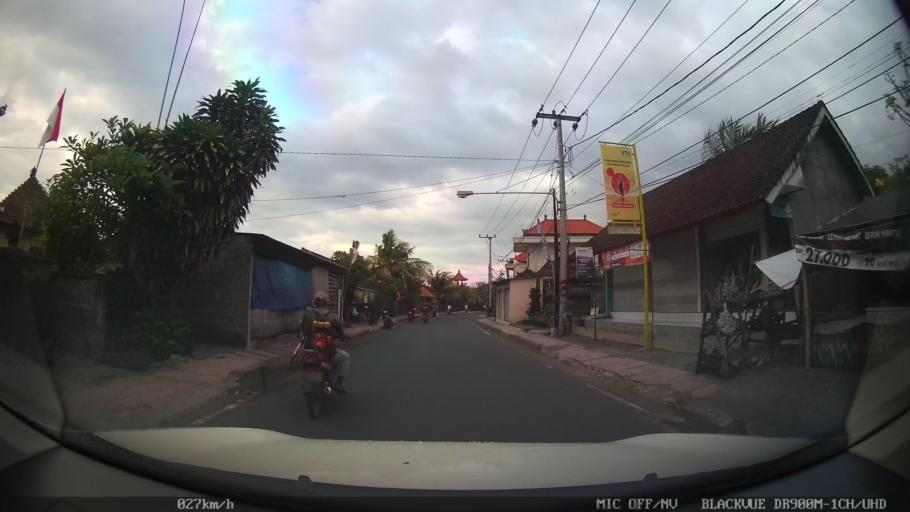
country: ID
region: Bali
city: Banjar Pasekan
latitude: -8.6315
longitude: 115.2846
